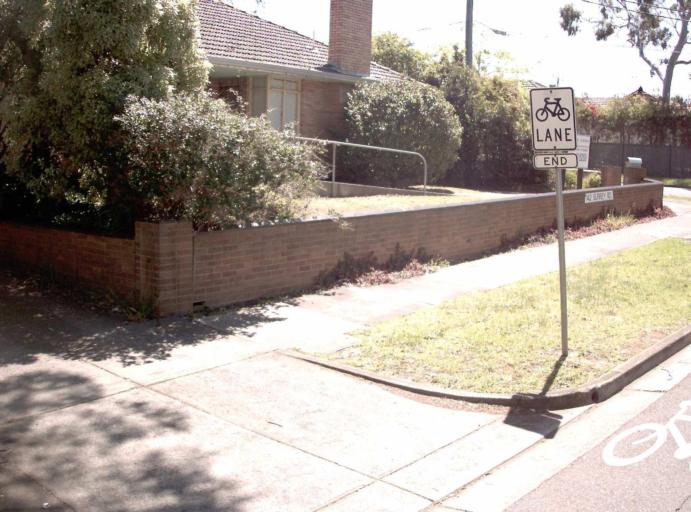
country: AU
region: Victoria
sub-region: Whitehorse
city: Blackburn North
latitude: -37.8121
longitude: 145.1575
